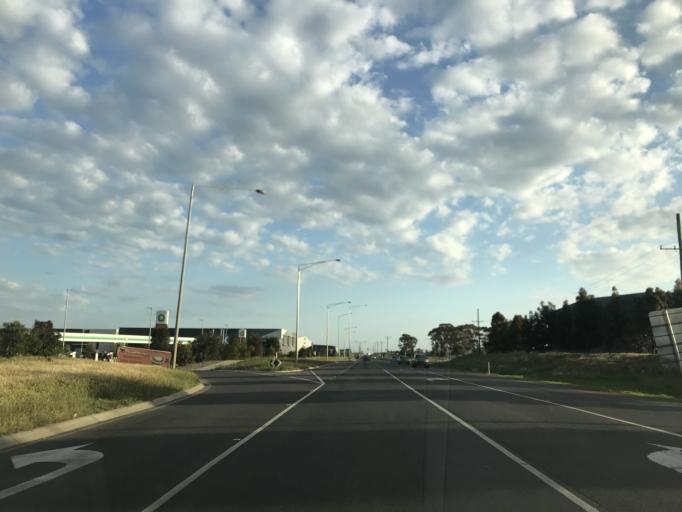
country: AU
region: Victoria
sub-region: Wyndham
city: Truganina
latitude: -37.8119
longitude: 144.7509
